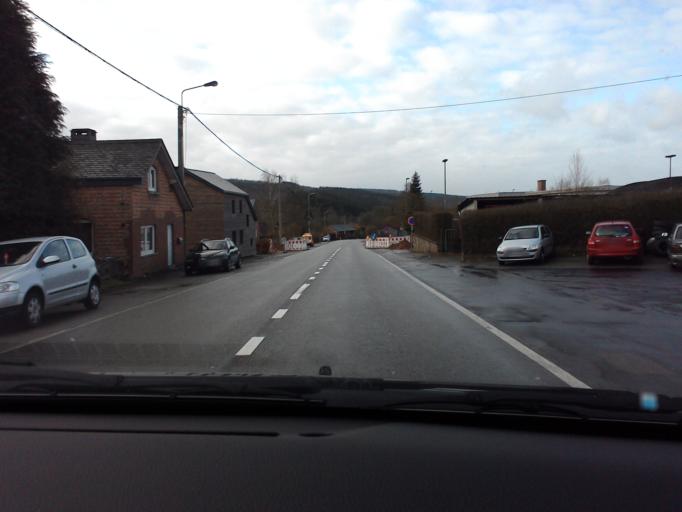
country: BE
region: Wallonia
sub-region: Province de Liege
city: Stavelot
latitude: 50.3855
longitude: 5.9180
